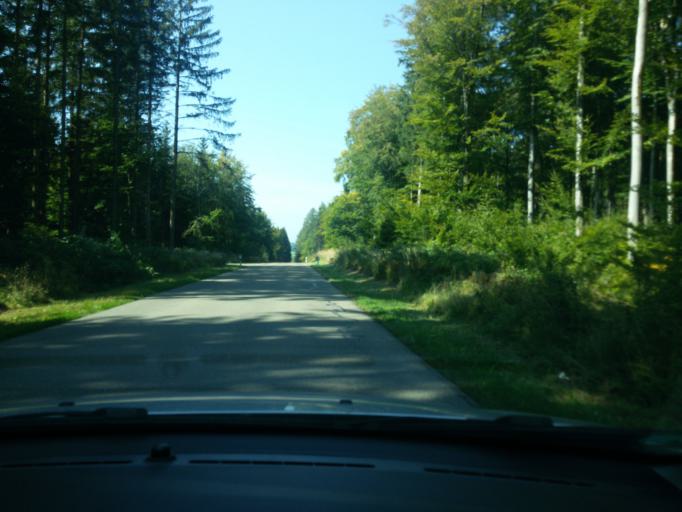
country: DE
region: Bavaria
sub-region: Swabia
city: Scherstetten
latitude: 48.1840
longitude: 10.6637
